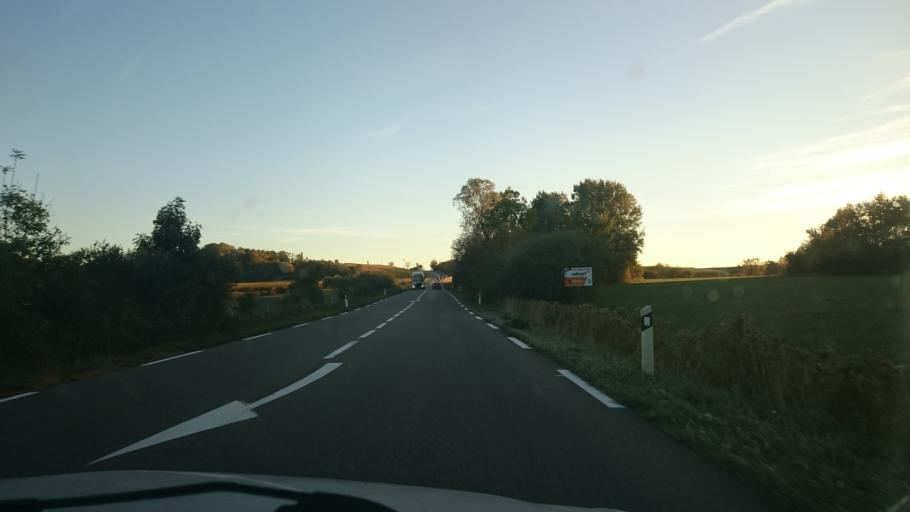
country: FR
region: Franche-Comte
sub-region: Departement du Jura
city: Arbois
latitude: 46.9386
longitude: 5.7780
